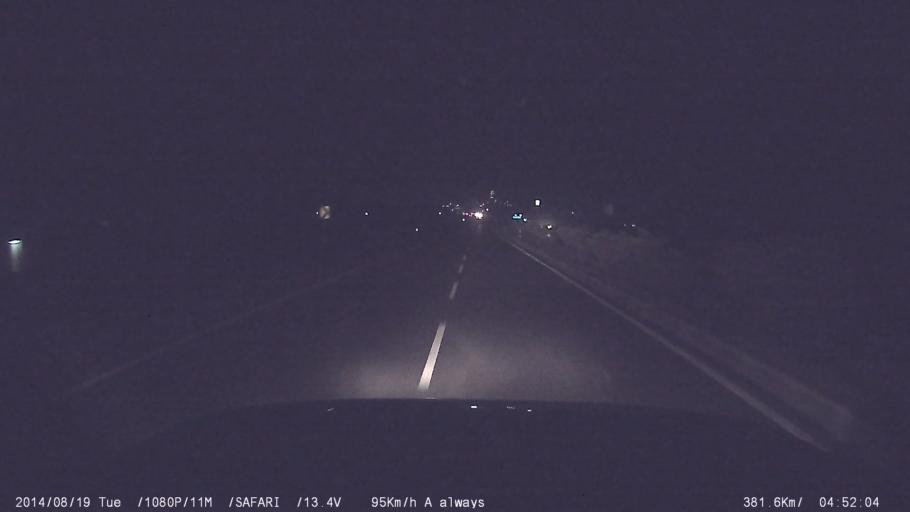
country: IN
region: Tamil Nadu
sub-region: Erode
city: Bhavani
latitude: 11.4547
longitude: 77.8006
